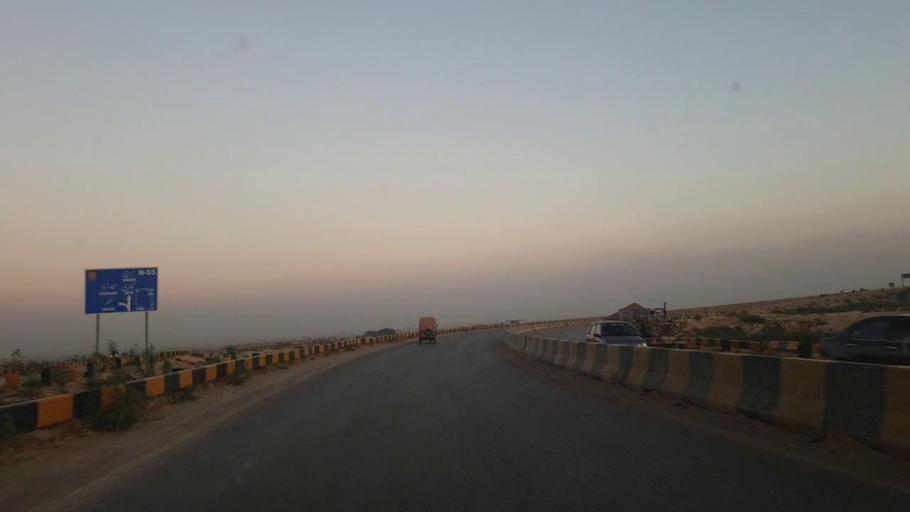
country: PK
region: Sindh
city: Jamshoro
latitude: 25.4042
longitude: 68.2706
